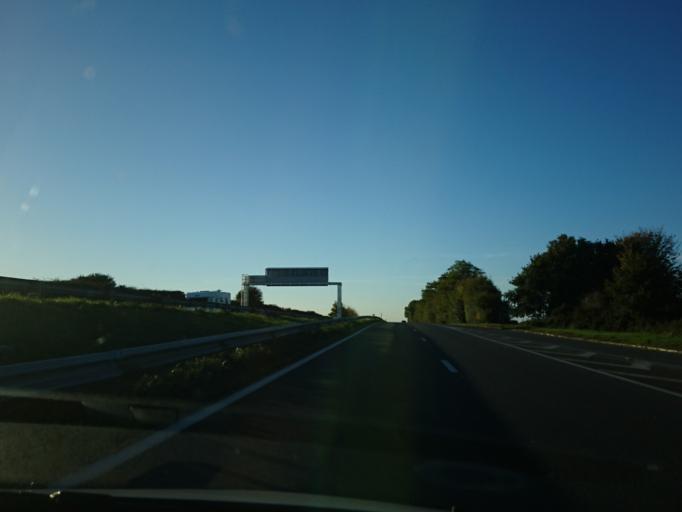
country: FR
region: Brittany
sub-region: Departement des Cotes-d'Armor
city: Tremuson
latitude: 48.5246
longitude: -2.8895
